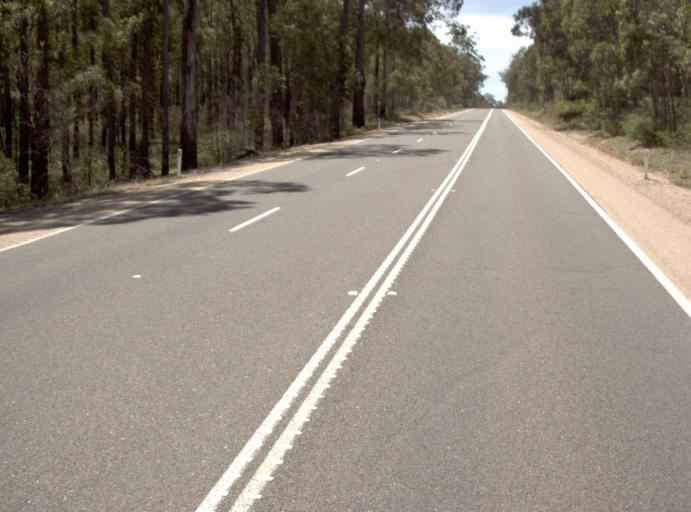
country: AU
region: Victoria
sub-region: East Gippsland
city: Bairnsdale
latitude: -37.7441
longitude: 147.7621
